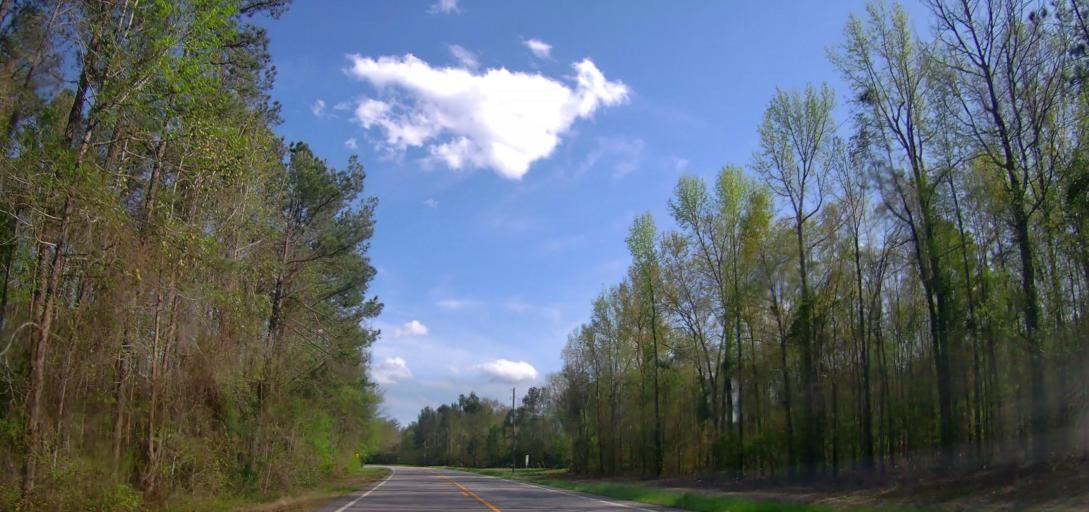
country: US
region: Georgia
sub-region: Baldwin County
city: Hardwick
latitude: 33.0613
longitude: -83.1308
